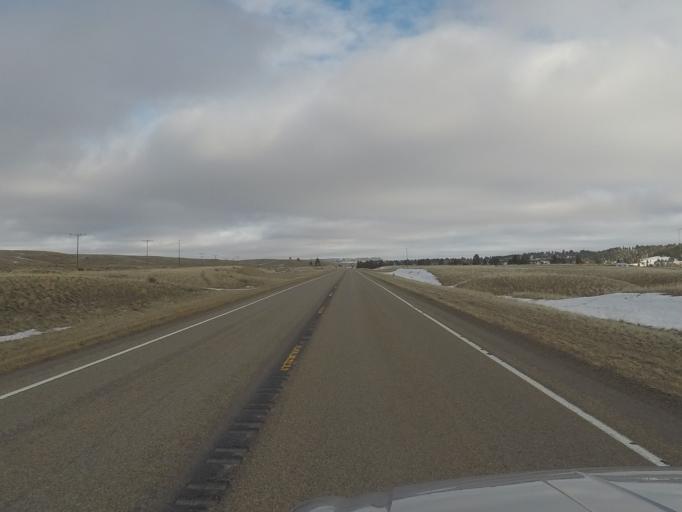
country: US
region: Montana
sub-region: Golden Valley County
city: Ryegate
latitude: 46.3050
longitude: -109.3444
